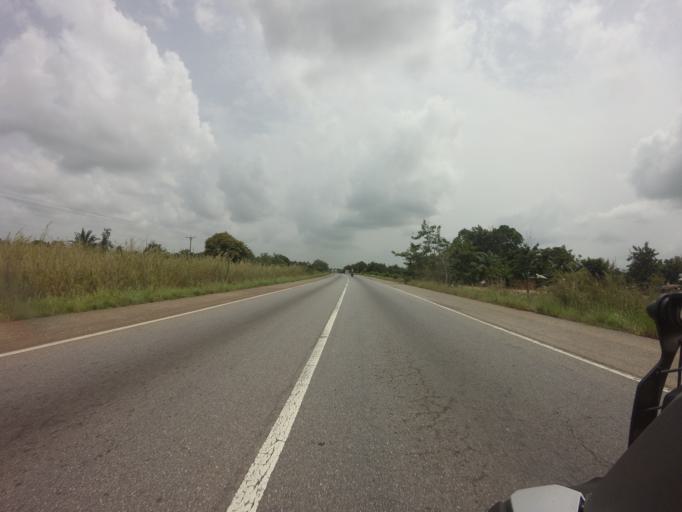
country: GH
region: Volta
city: Keta
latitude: 6.0503
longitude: 0.7252
